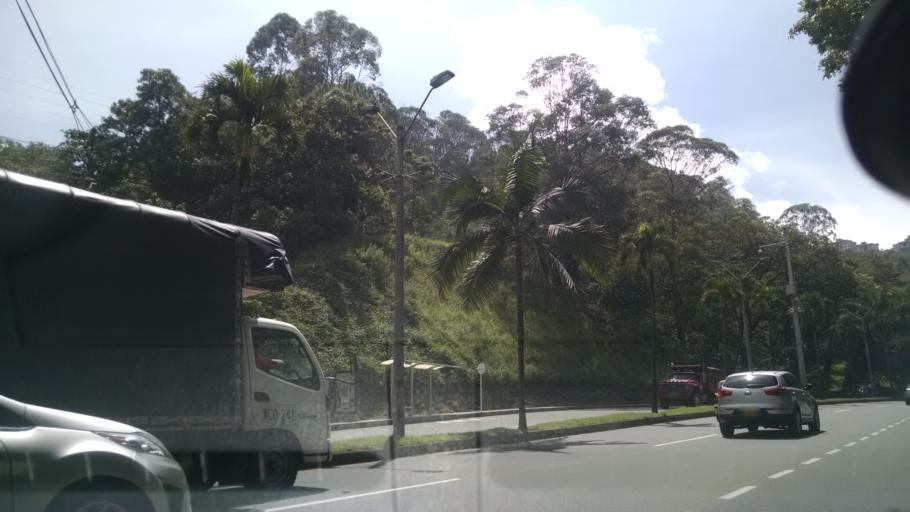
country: CO
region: Antioquia
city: Medellin
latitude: 6.2334
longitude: -75.5672
